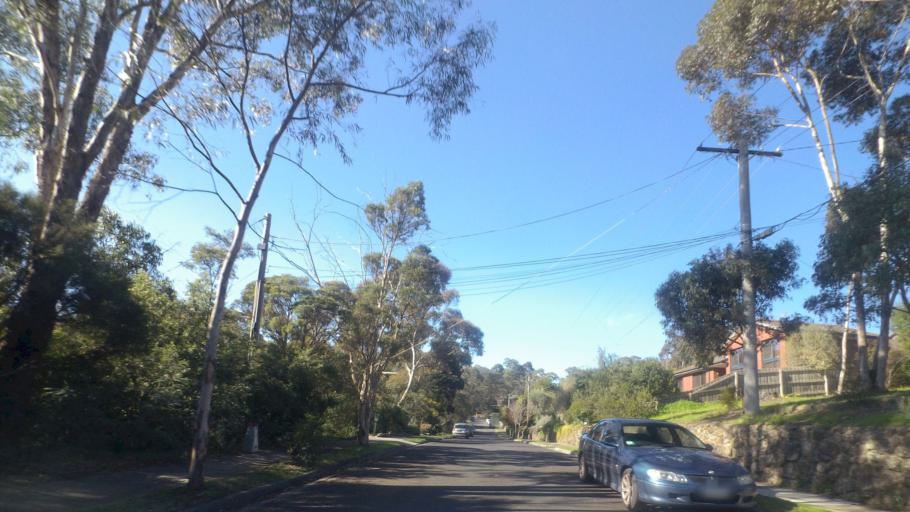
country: AU
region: Victoria
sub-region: Nillumbik
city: Eltham
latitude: -37.7235
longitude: 145.1526
